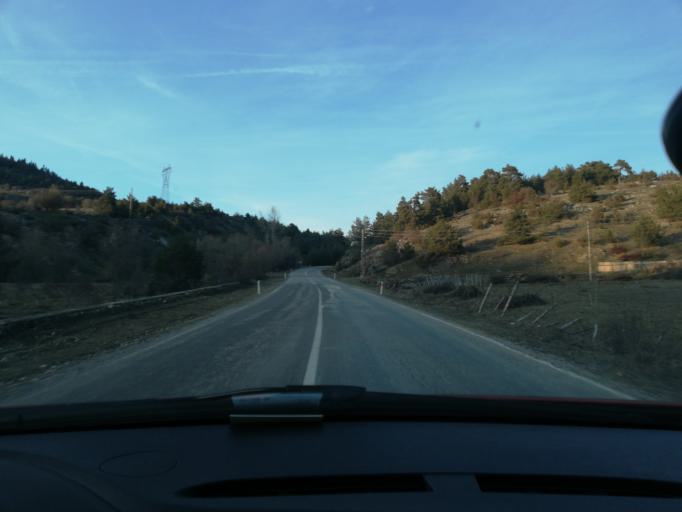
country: TR
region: Kastamonu
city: Agli
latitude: 41.7066
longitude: 33.6515
